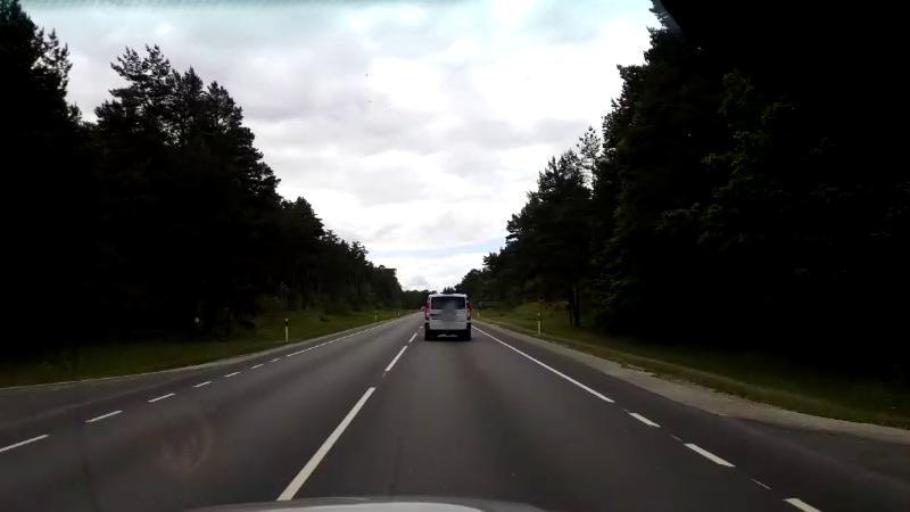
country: EE
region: Paernumaa
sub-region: Paernu linn
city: Parnu
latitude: 58.2004
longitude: 24.4858
